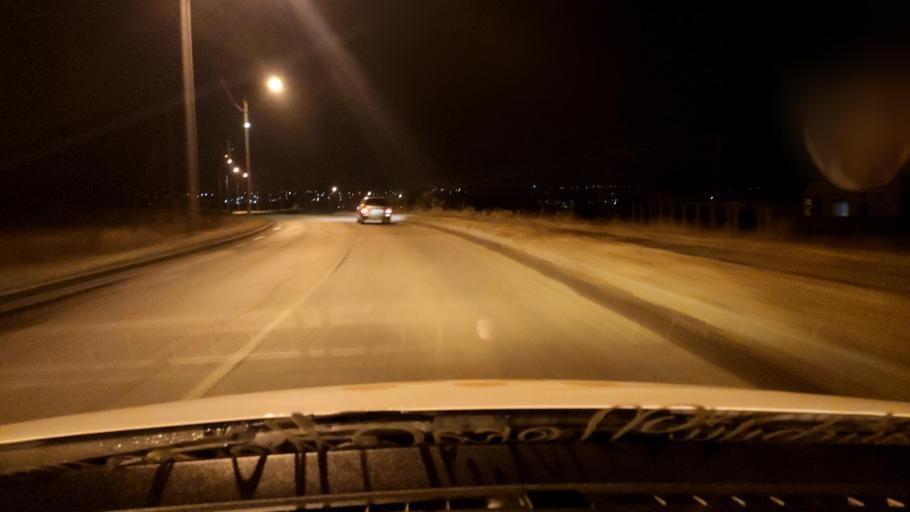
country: RU
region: Voronezj
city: Semiluki
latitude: 51.6650
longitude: 39.0393
